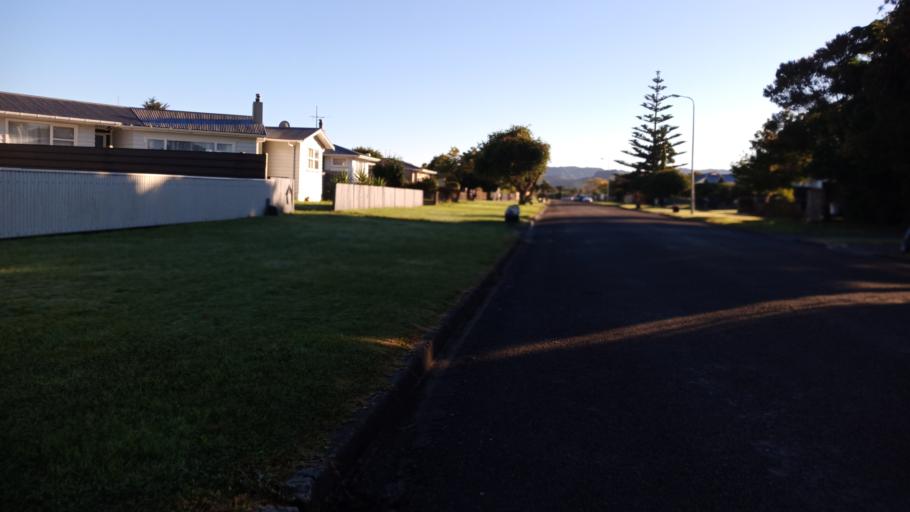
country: NZ
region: Gisborne
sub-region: Gisborne District
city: Gisborne
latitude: -38.6610
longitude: 178.0011
